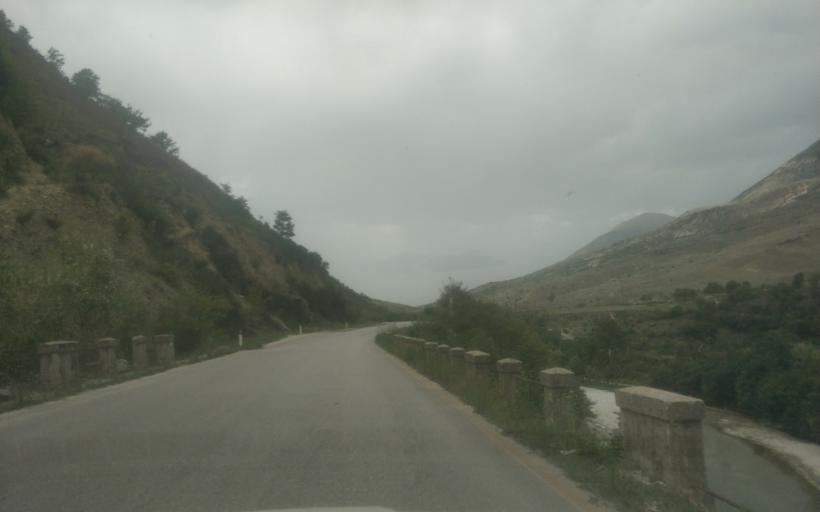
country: AL
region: Gjirokaster
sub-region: Rrethi i Gjirokastres
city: Picar
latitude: 40.2305
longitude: 20.0833
